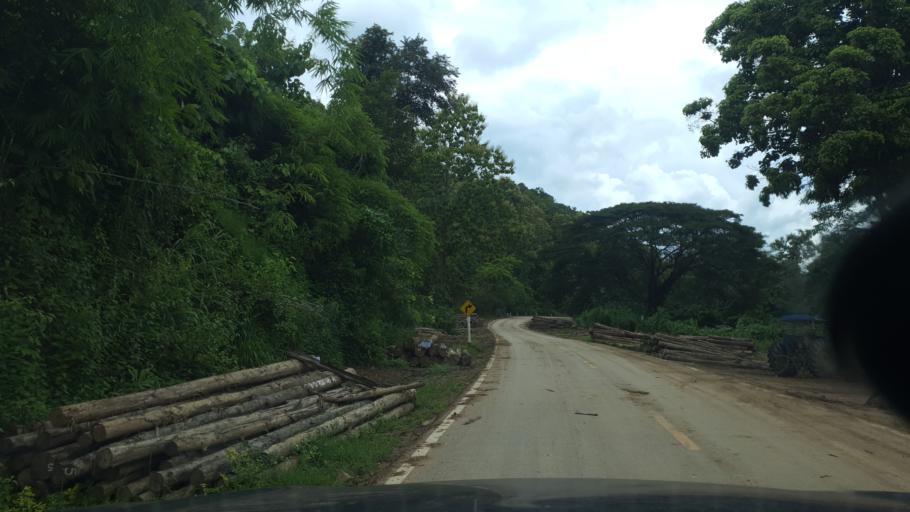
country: TH
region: Lampang
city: Hang Chat
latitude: 18.3737
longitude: 99.2598
